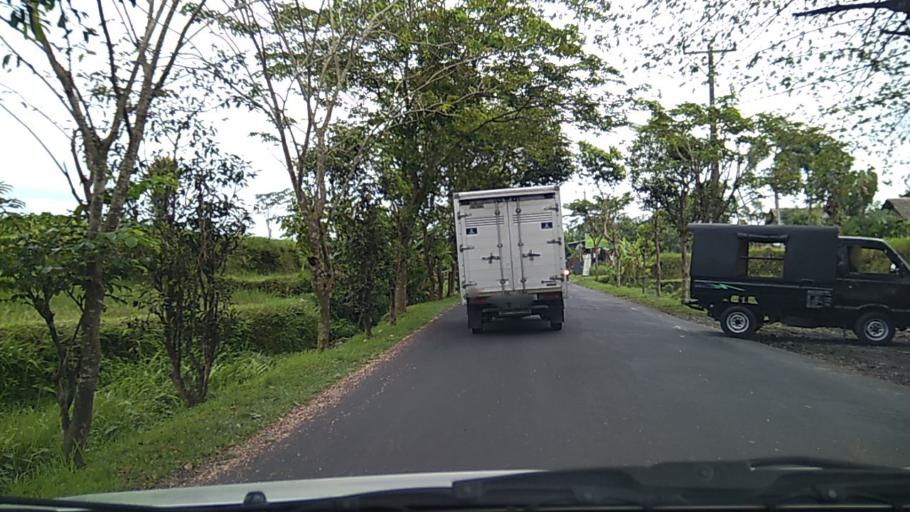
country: ID
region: Bali
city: Banjar Kembangsari
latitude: -8.5016
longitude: 115.2102
